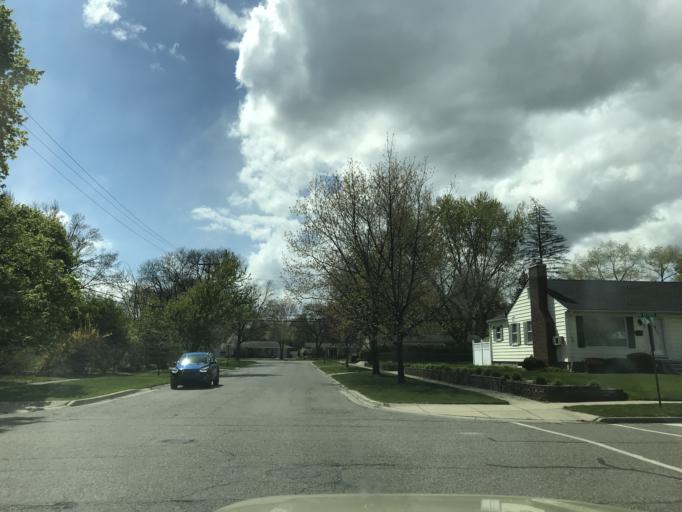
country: US
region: Michigan
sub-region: Wayne County
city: Plymouth
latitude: 42.3777
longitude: -83.4791
